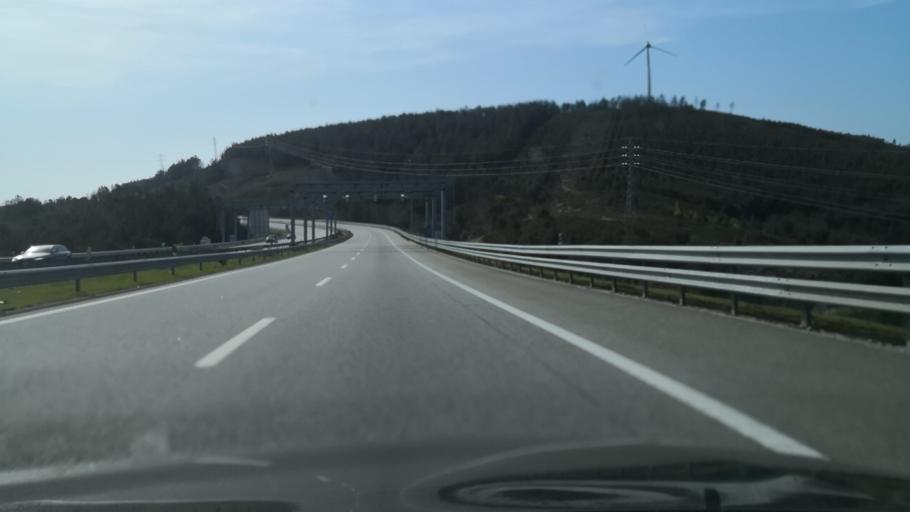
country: PT
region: Aveiro
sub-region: Sever do Vouga
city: Sever do Vouga
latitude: 40.6692
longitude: -8.3453
